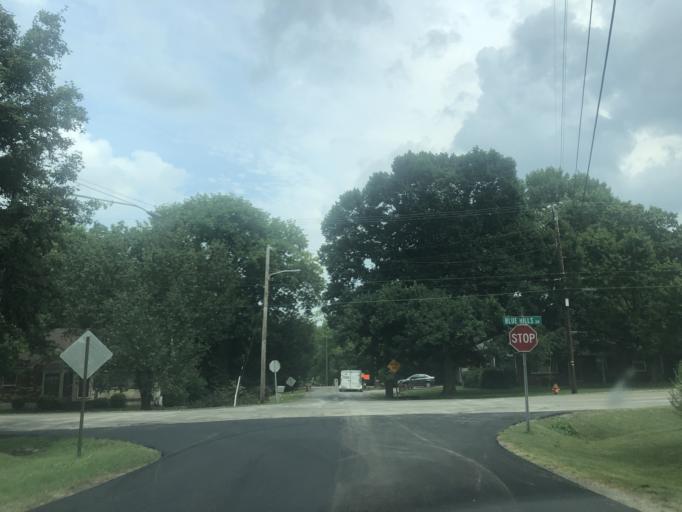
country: US
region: Tennessee
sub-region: Davidson County
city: Lakewood
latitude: 36.1623
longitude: -86.6848
